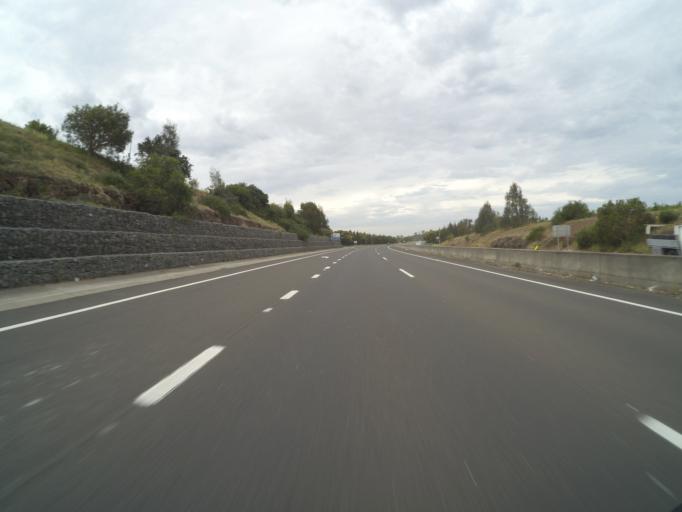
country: AU
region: New South Wales
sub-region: Kiama
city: Kiama
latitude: -34.6358
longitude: 150.8323
